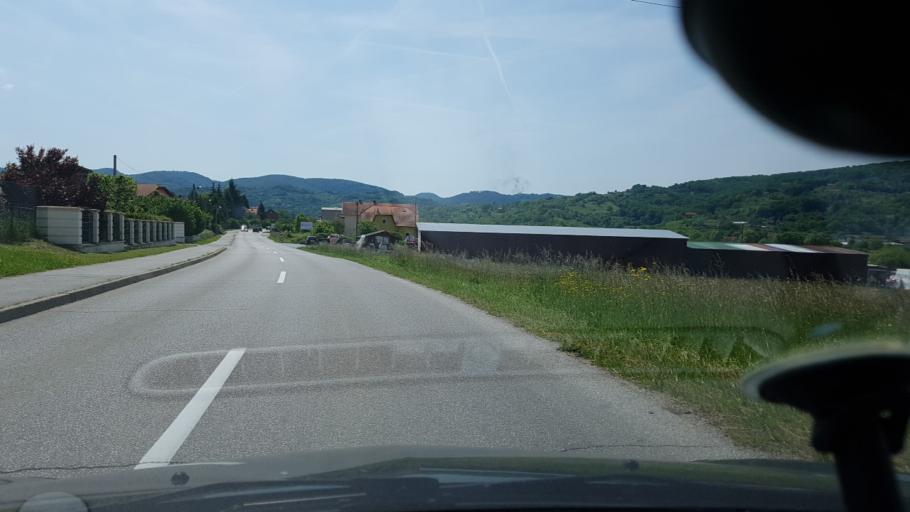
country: HR
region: Krapinsko-Zagorska
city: Marija Bistrica
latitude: 46.0134
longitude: 16.1071
